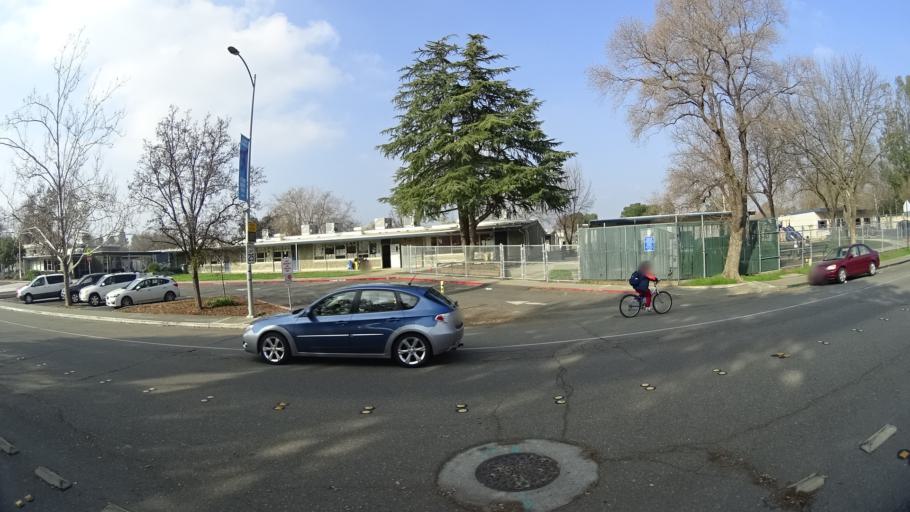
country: US
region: California
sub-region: Yolo County
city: Davis
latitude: 38.5565
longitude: -121.7451
